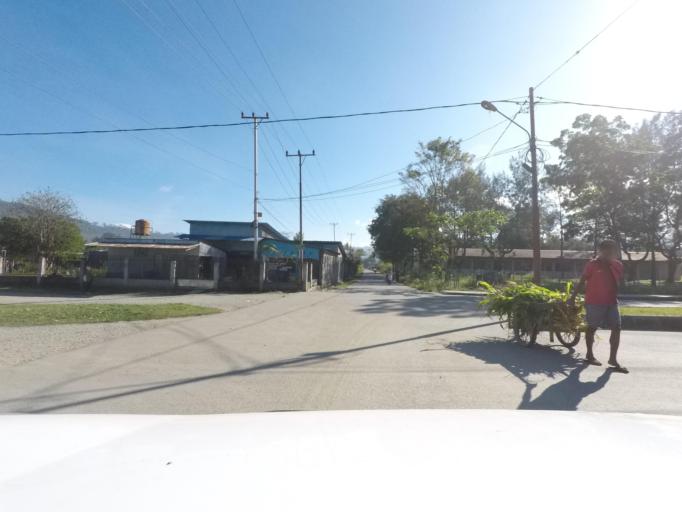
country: TL
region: Ermera
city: Gleno
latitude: -8.7228
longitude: 125.4315
